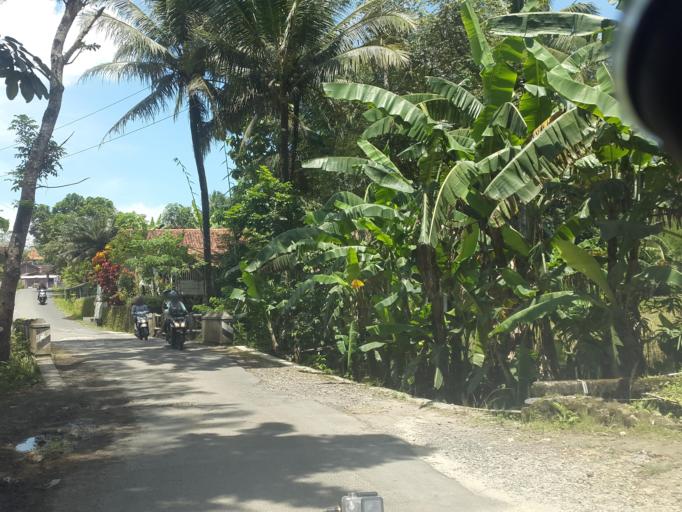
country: ID
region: Central Java
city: Sangkalputung
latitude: -7.4135
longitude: 109.0509
